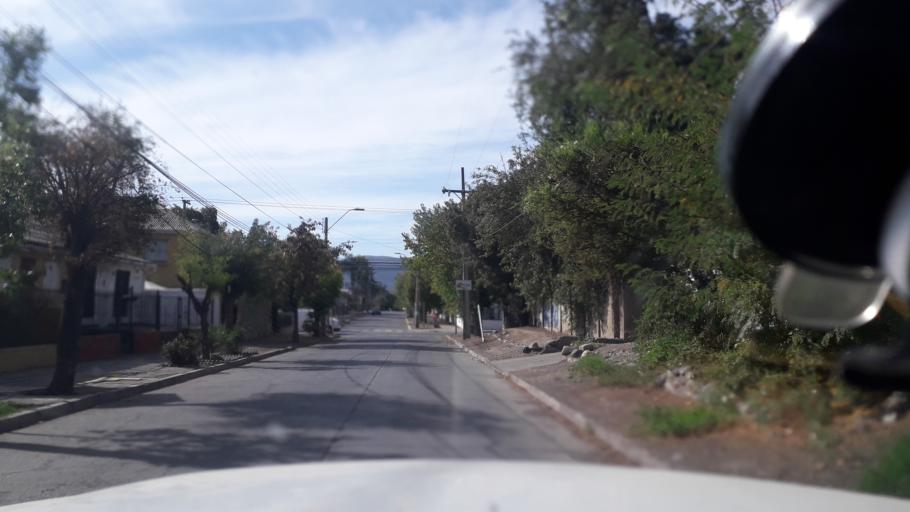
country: CL
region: Valparaiso
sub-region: Provincia de San Felipe
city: San Felipe
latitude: -32.7529
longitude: -70.7160
